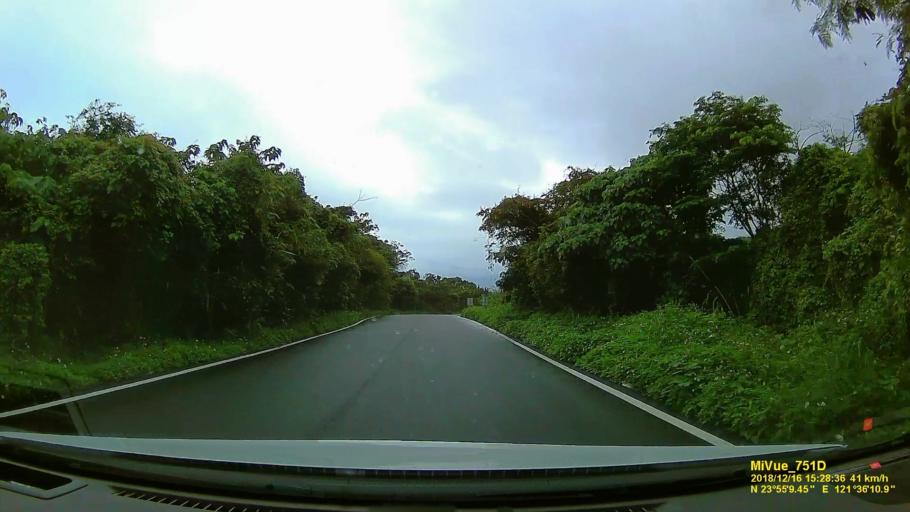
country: TW
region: Taiwan
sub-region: Hualien
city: Hualian
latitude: 23.9189
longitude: 121.6030
